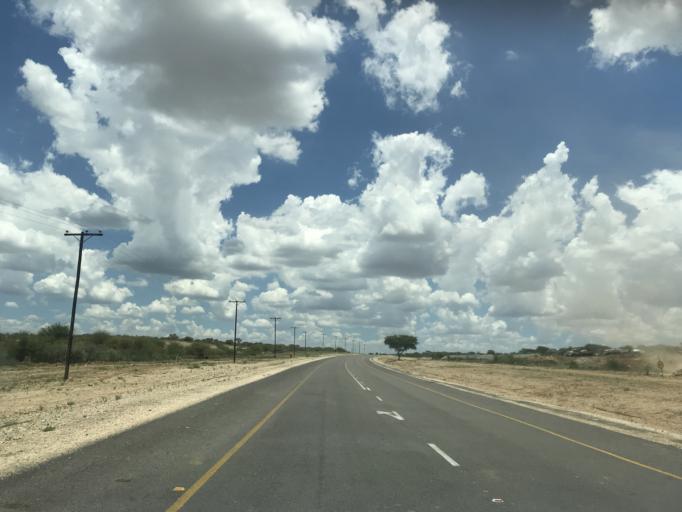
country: BW
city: Mabuli
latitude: -25.7838
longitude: 24.9104
